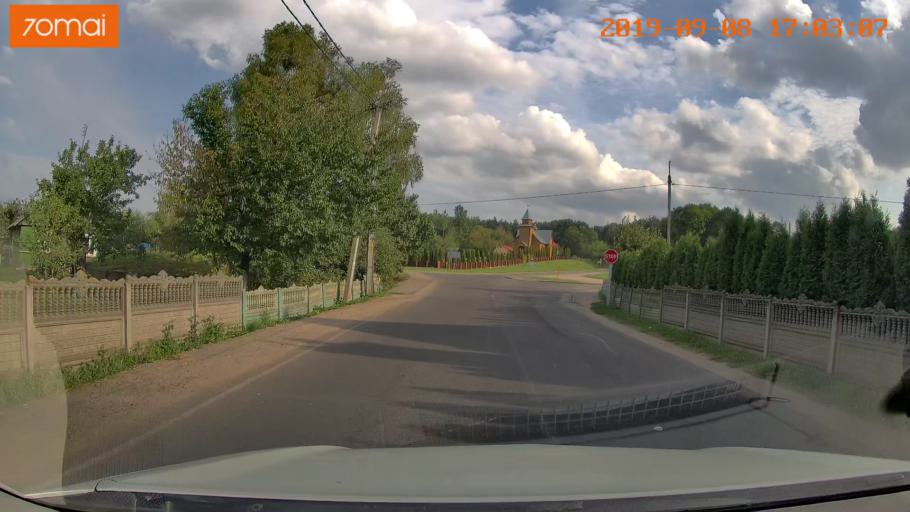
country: BY
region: Grodnenskaya
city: Hrodna
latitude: 53.6977
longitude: 23.9420
